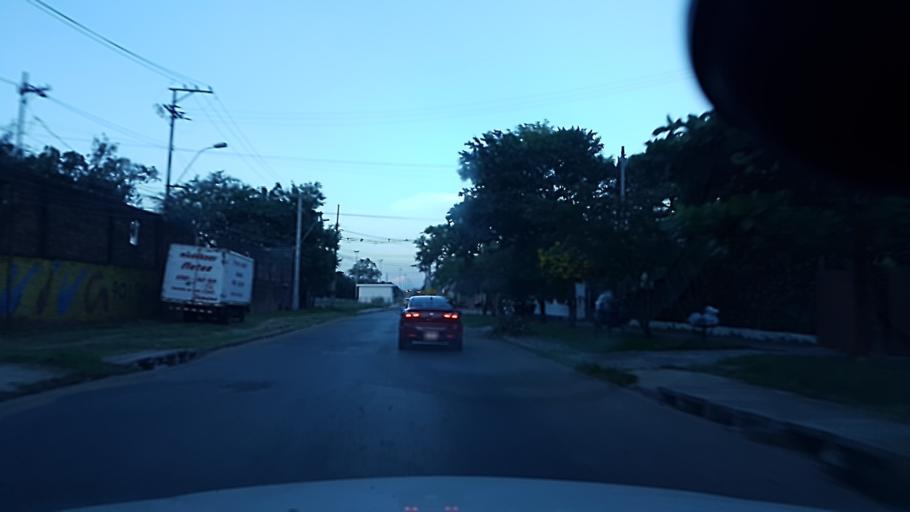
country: PY
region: Asuncion
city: Asuncion
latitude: -25.2570
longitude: -57.5674
